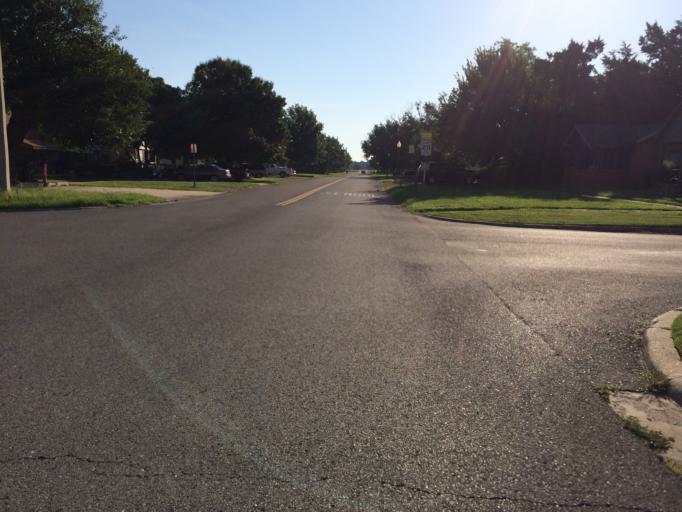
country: US
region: Oklahoma
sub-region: Cleveland County
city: Norman
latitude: 35.2238
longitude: -97.4366
